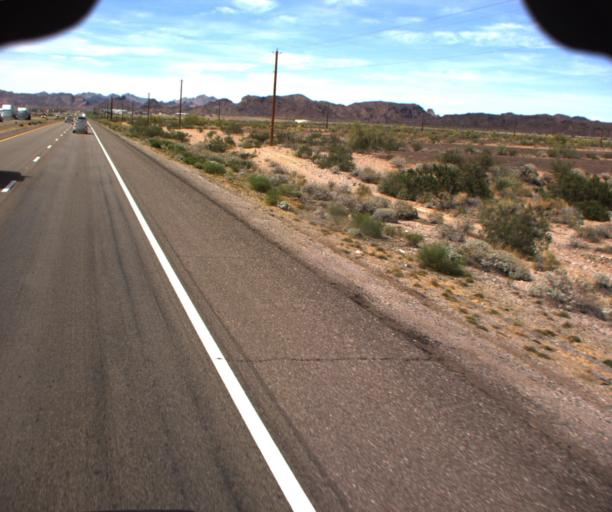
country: US
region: Arizona
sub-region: Mohave County
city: Desert Hills
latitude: 34.5495
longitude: -114.3562
